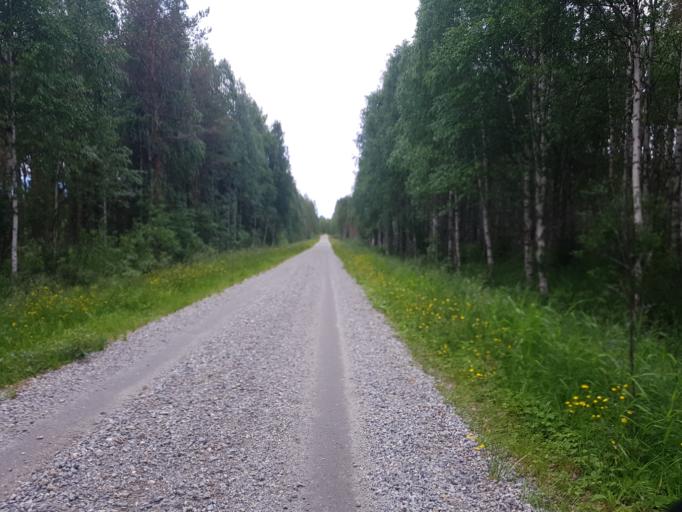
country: FI
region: Kainuu
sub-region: Kehys-Kainuu
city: Kuhmo
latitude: 64.4517
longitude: 29.6949
